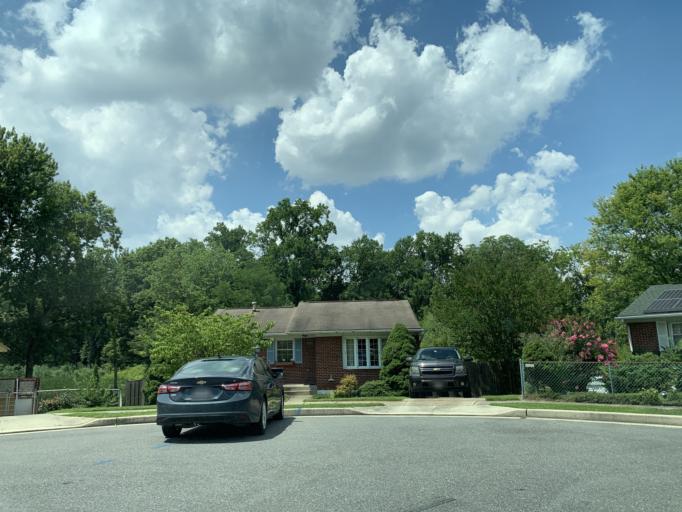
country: US
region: Maryland
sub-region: Baltimore County
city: Essex
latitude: 39.3096
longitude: -76.4676
